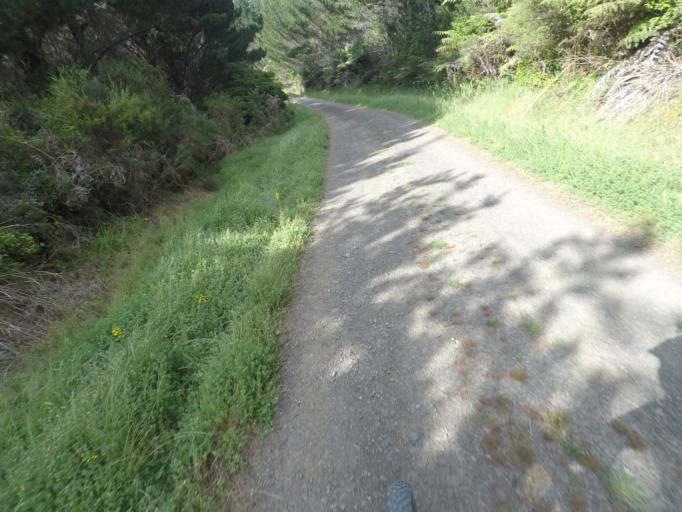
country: NZ
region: Auckland
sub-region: Auckland
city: Muriwai Beach
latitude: -36.7471
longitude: 174.5636
